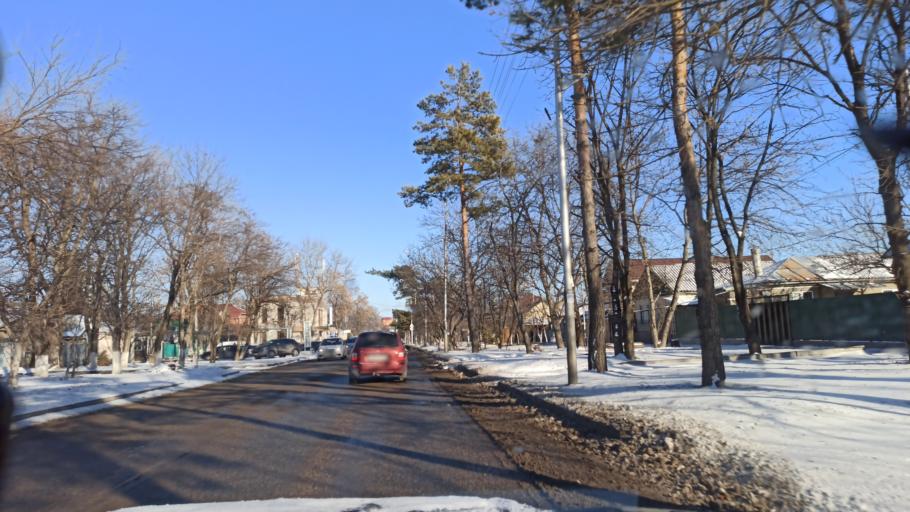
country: RU
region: Stavropol'skiy
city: Yessentukskaya
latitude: 44.0416
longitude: 42.8810
